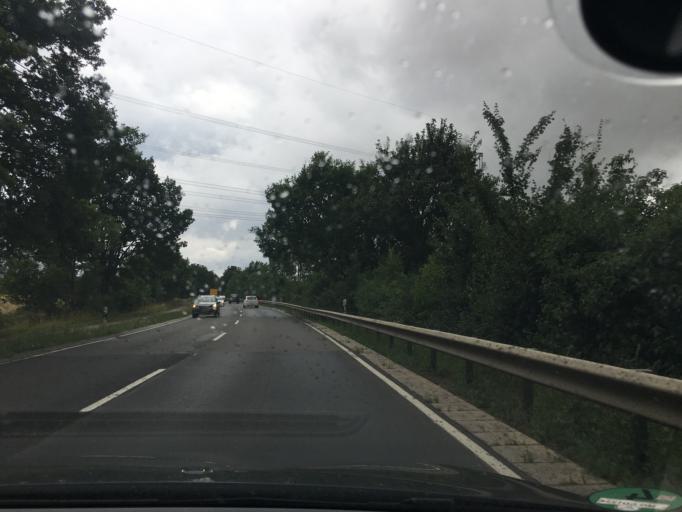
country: DE
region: North Rhine-Westphalia
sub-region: Regierungsbezirk Koln
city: Kreuzau
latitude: 50.7519
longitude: 6.5365
